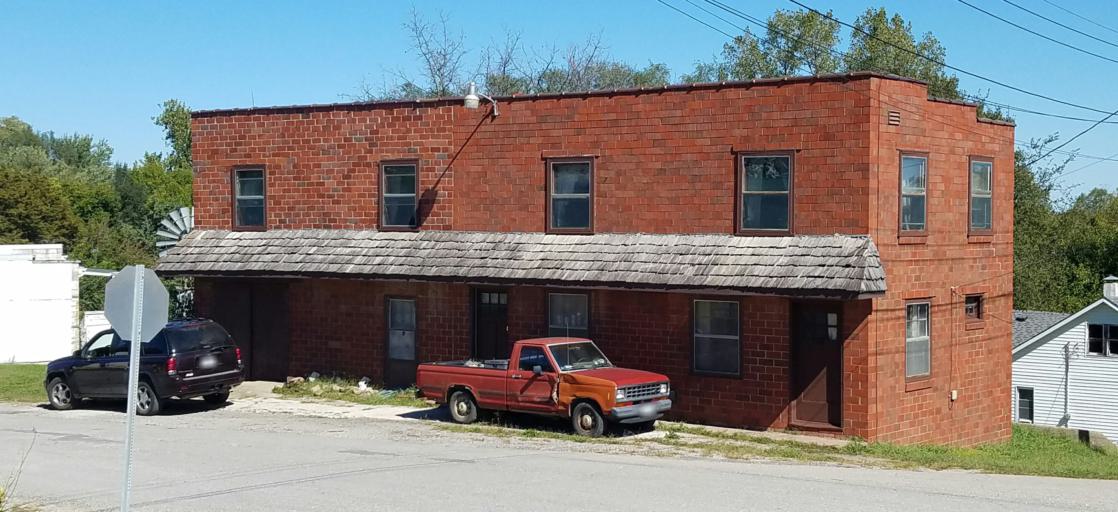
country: US
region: Missouri
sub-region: Worth County
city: Grant City
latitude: 40.4856
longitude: -94.4124
